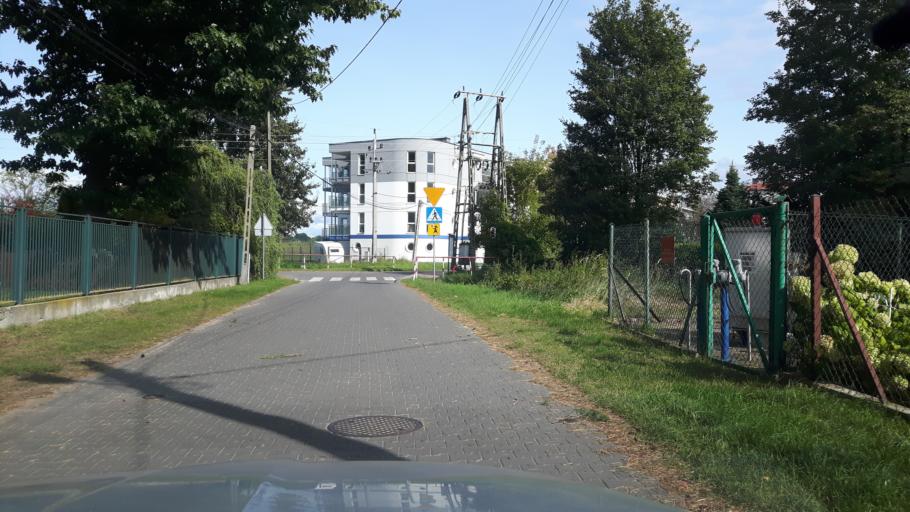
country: PL
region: Masovian Voivodeship
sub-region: Powiat legionowski
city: Wieliszew
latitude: 52.4563
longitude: 21.0045
